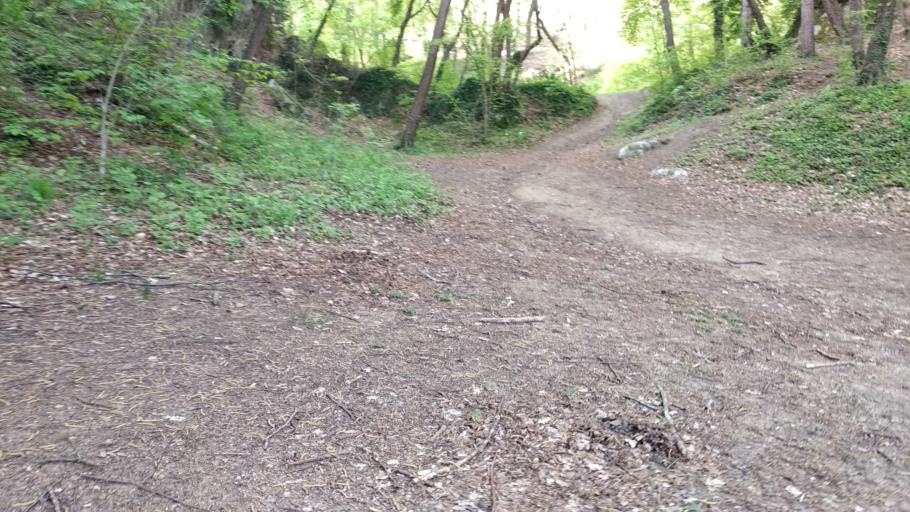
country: IT
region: Emilia-Romagna
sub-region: Provincia di Ravenna
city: Fognano
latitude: 44.2257
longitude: 11.7400
